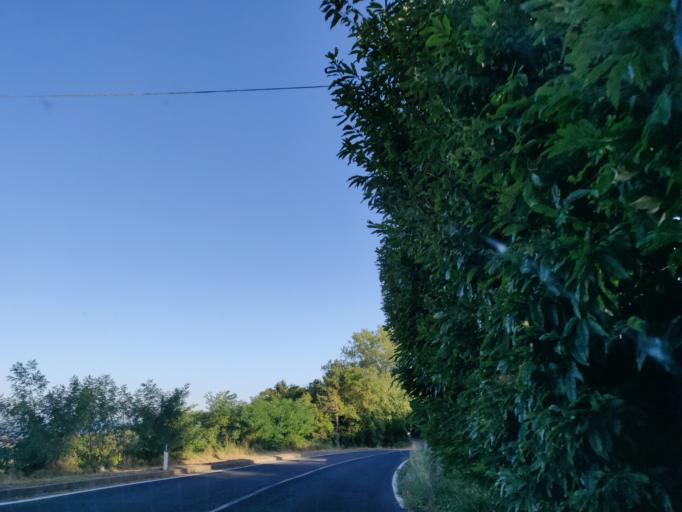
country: IT
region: Tuscany
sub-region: Provincia di Siena
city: Piancastagnaio
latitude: 42.8588
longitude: 11.6831
